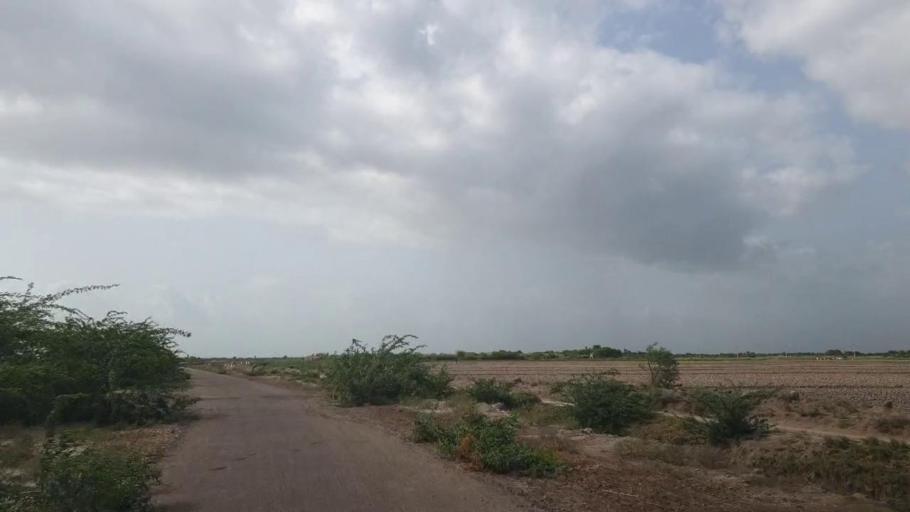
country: PK
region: Sindh
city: Kadhan
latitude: 24.5653
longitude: 69.0639
